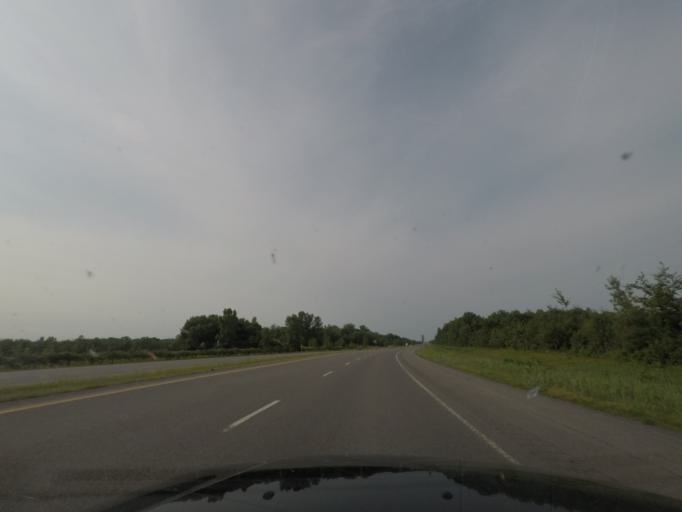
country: CA
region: Quebec
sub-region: Monteregie
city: Napierville
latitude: 45.2151
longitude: -73.4775
